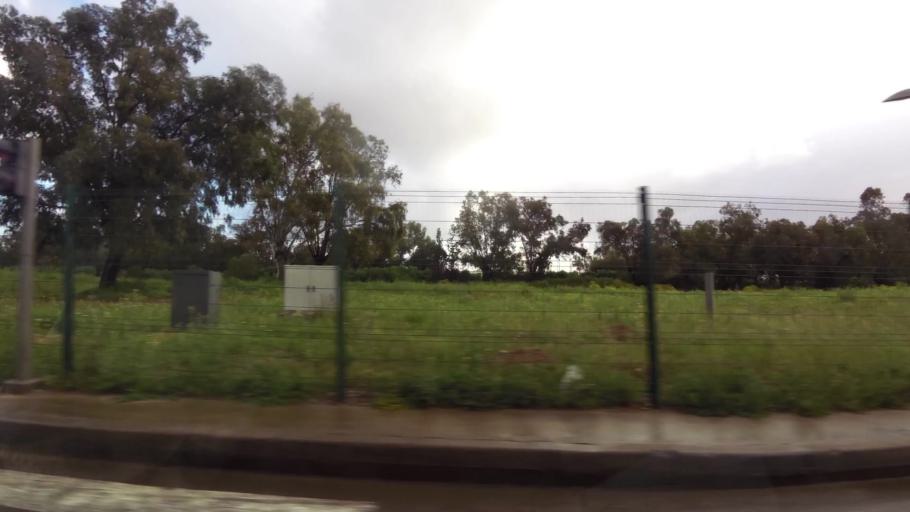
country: MA
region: Grand Casablanca
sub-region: Casablanca
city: Casablanca
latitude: 33.5620
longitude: -7.6527
